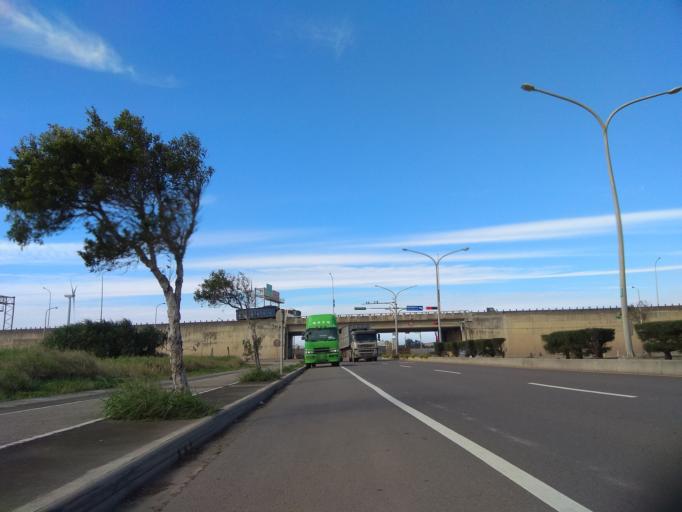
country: TW
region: Taiwan
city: Taoyuan City
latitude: 25.0788
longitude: 121.1692
